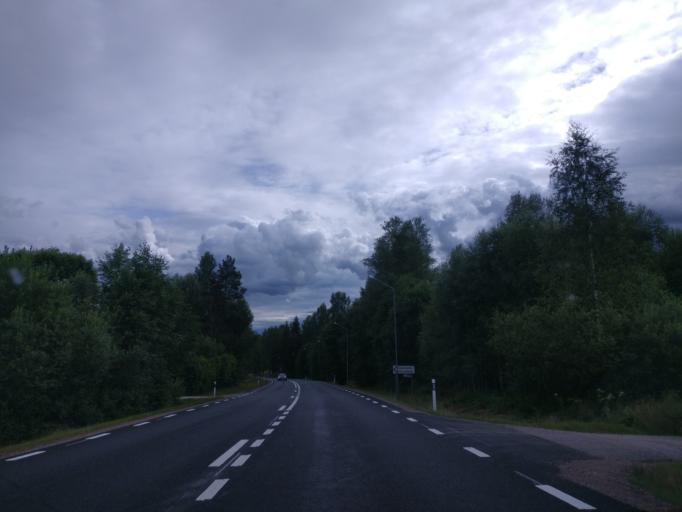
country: SE
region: Vaermland
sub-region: Hagfors Kommun
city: Ekshaerad
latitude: 60.0689
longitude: 13.5497
